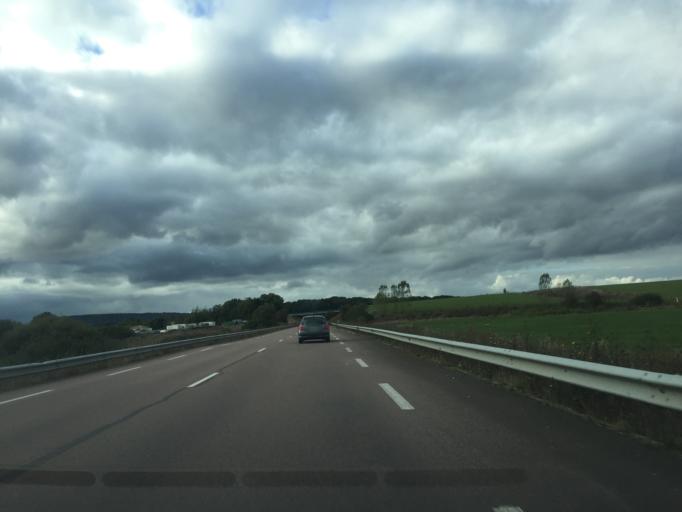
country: FR
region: Lorraine
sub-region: Departement des Vosges
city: Chatenois
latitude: 48.2950
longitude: 5.8884
